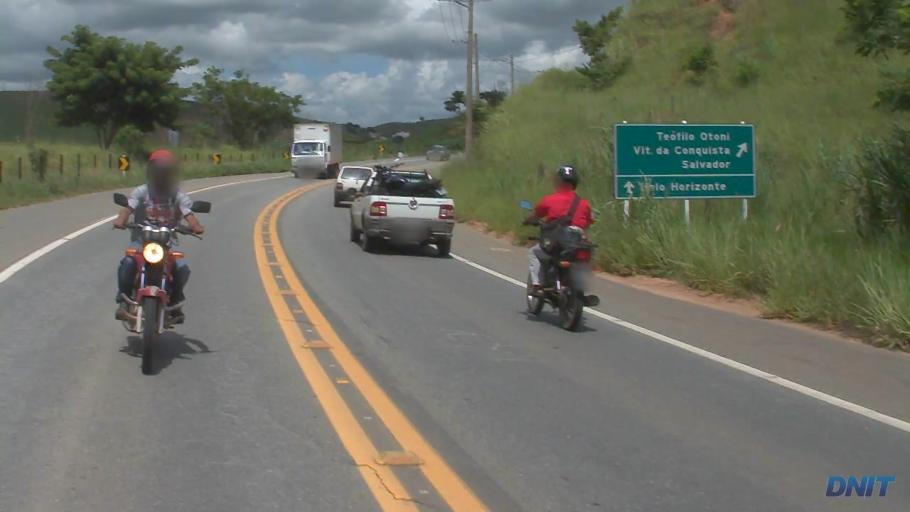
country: BR
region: Minas Gerais
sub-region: Governador Valadares
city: Governador Valadares
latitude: -18.8810
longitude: -41.9945
